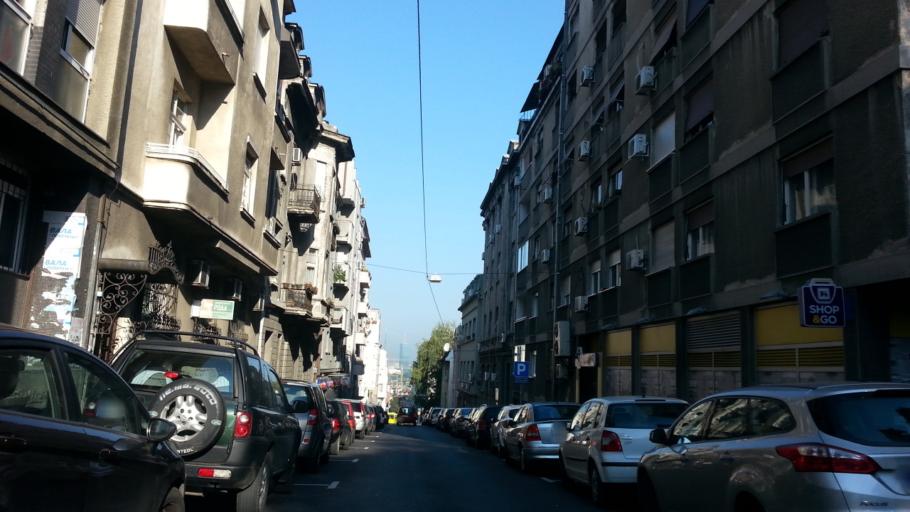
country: RS
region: Central Serbia
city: Belgrade
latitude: 44.8027
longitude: 20.4595
